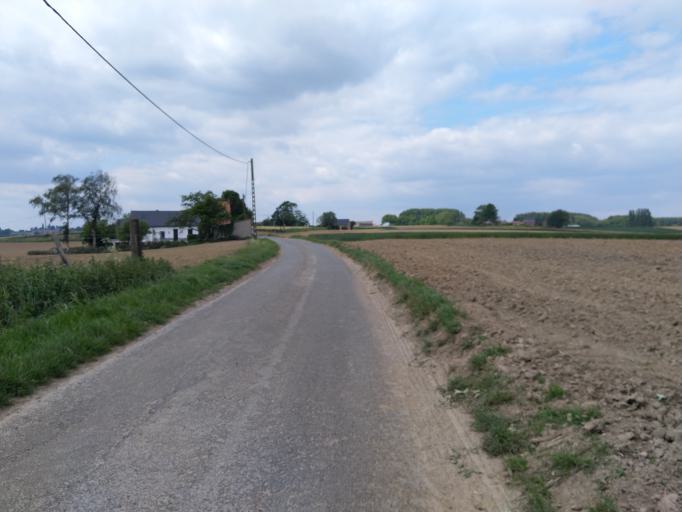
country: BE
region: Wallonia
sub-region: Province du Hainaut
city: Enghien
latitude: 50.6491
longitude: 4.0275
